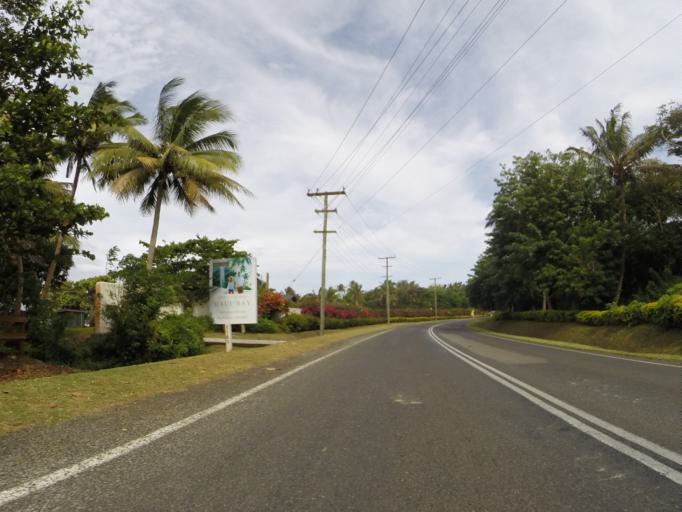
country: FJ
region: Western
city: Nadi
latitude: -18.2027
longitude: 177.6779
